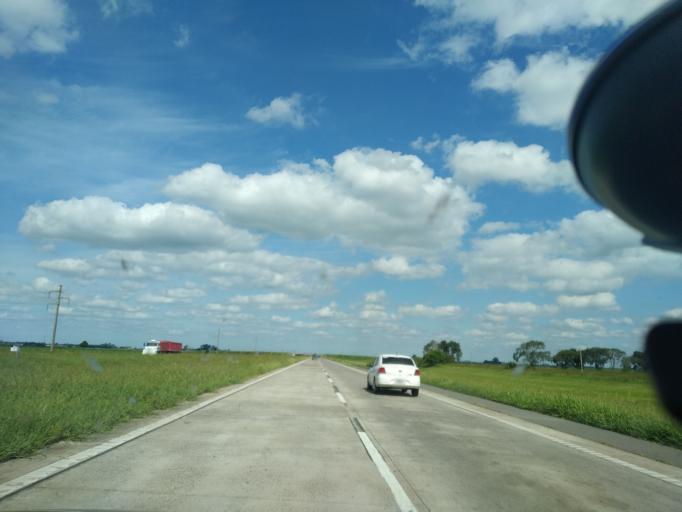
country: AR
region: Santa Fe
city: Canada de Gomez
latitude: -32.8628
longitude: -61.2968
